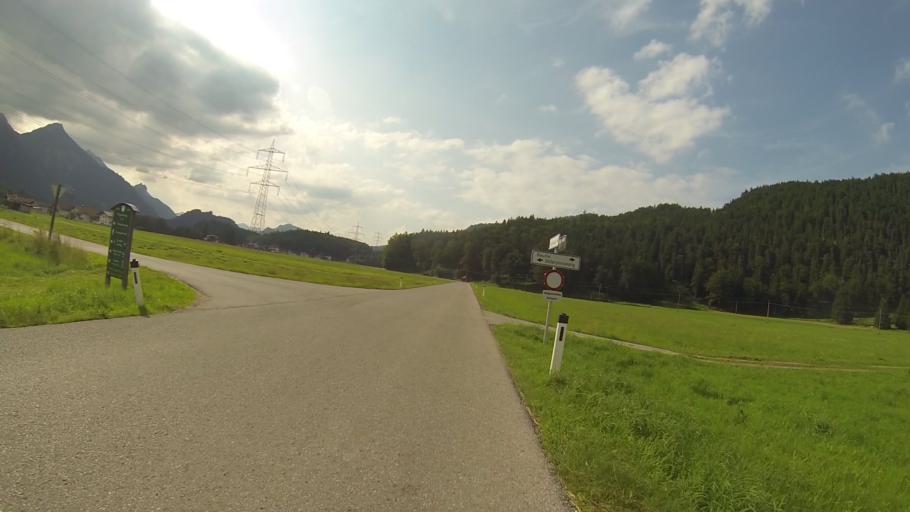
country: AT
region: Tyrol
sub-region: Politischer Bezirk Reutte
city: Pflach
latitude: 47.5328
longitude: 10.6973
